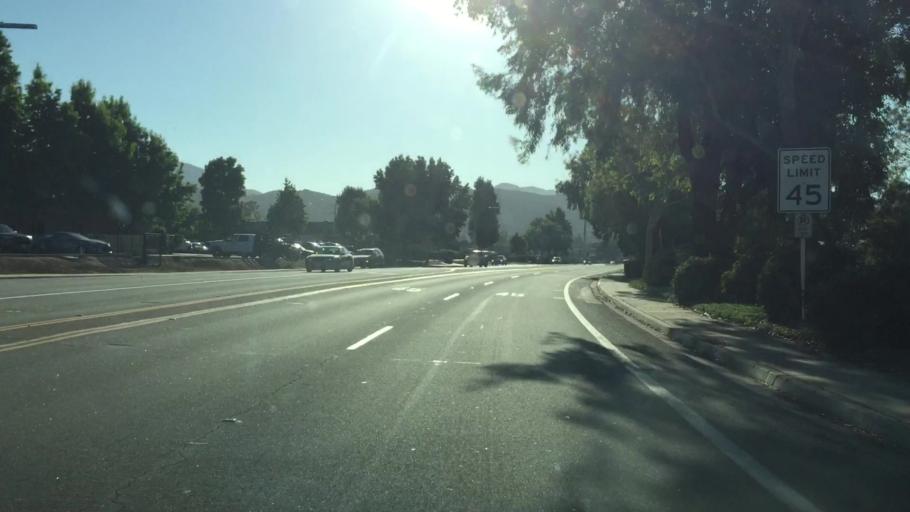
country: US
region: California
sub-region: San Diego County
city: Poway
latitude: 32.9782
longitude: -117.0361
